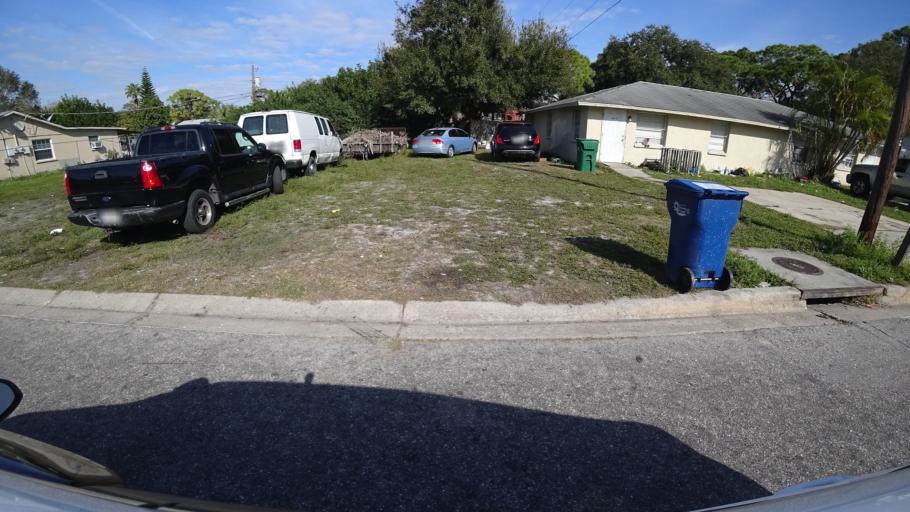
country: US
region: Florida
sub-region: Manatee County
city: Whitfield
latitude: 27.4342
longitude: -82.5671
